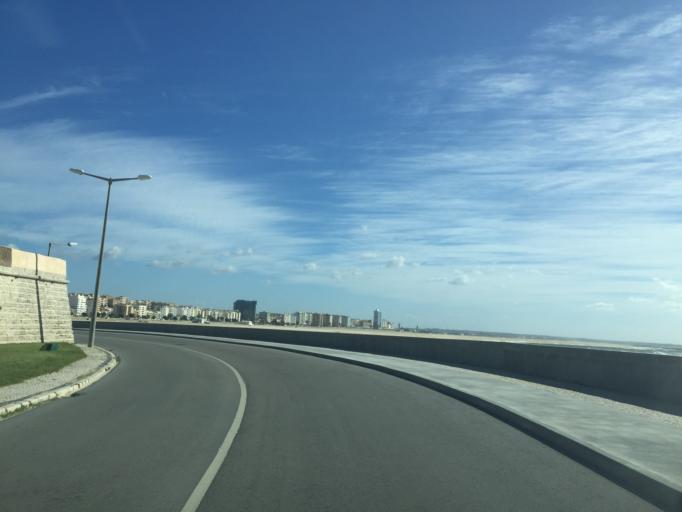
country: PT
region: Coimbra
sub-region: Figueira da Foz
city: Buarcos
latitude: 40.1643
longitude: -8.8798
